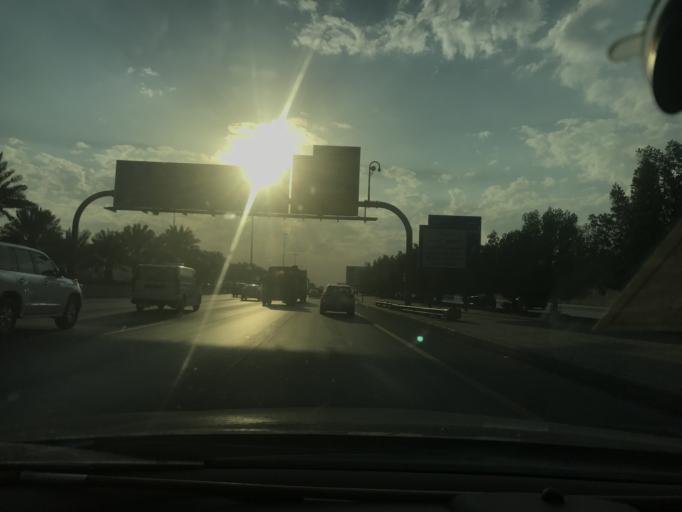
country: SA
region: Ar Riyad
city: Riyadh
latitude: 24.7813
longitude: 46.6955
